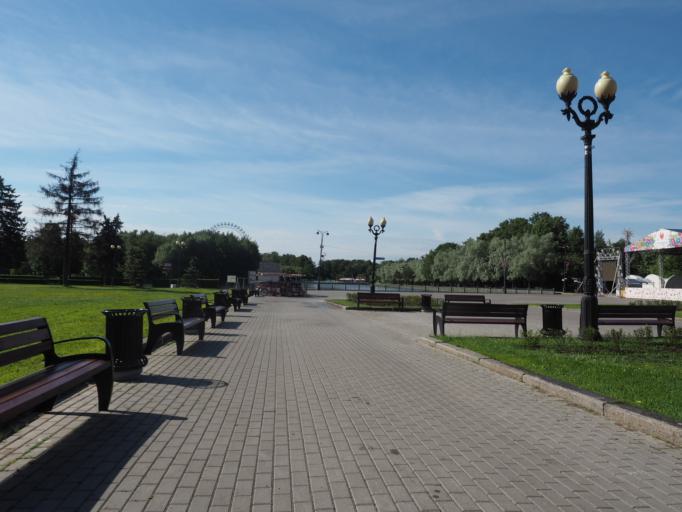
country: RU
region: Moscow
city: Ryazanskiy
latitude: 55.7740
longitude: 37.7493
